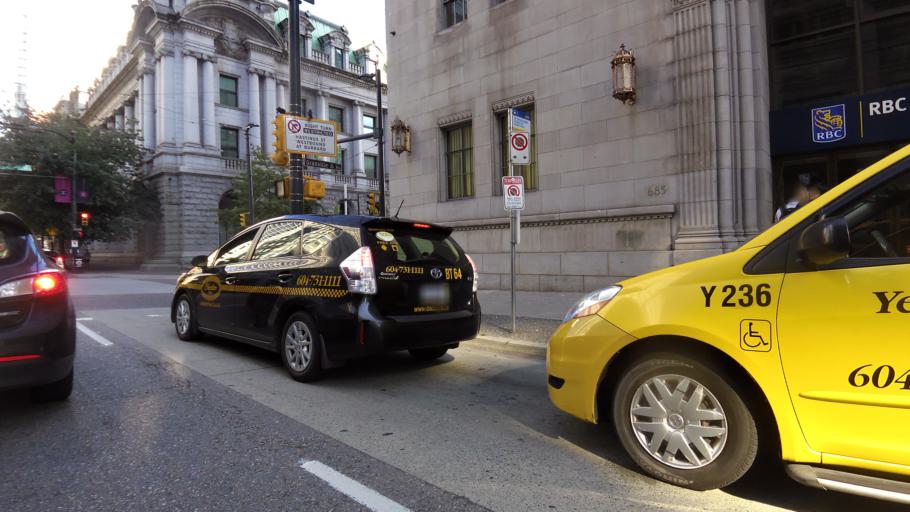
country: CA
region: British Columbia
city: West End
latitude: 49.2852
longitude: -123.1137
